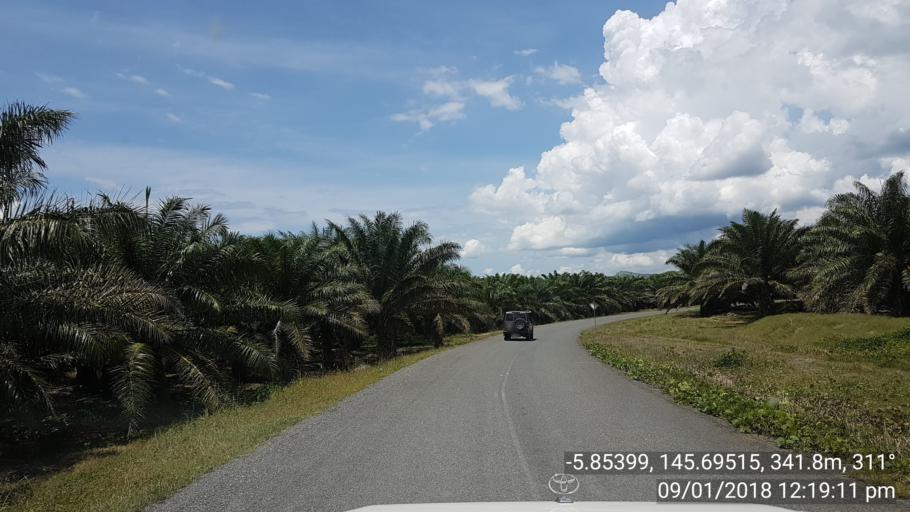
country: PG
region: Eastern Highlands
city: Goroka
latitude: -5.8541
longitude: 145.6953
